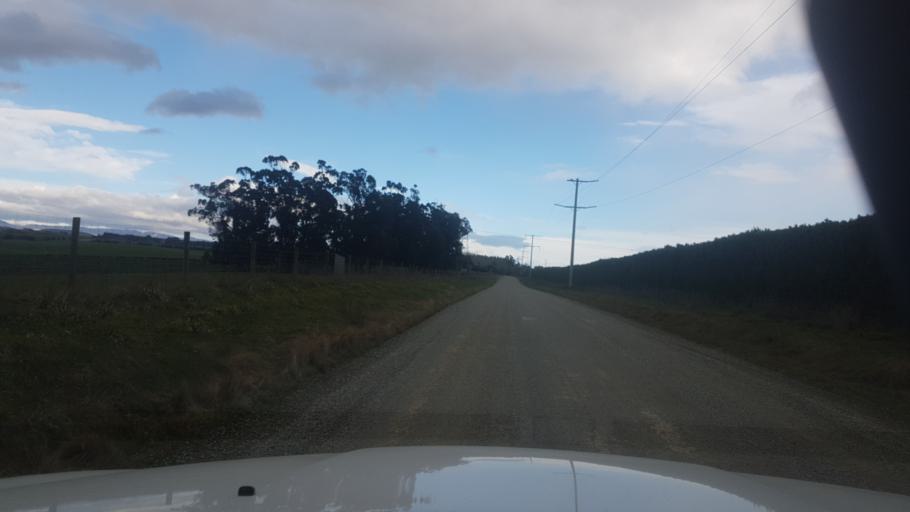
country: NZ
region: Canterbury
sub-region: Timaru District
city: Pleasant Point
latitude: -44.3541
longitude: 171.1341
